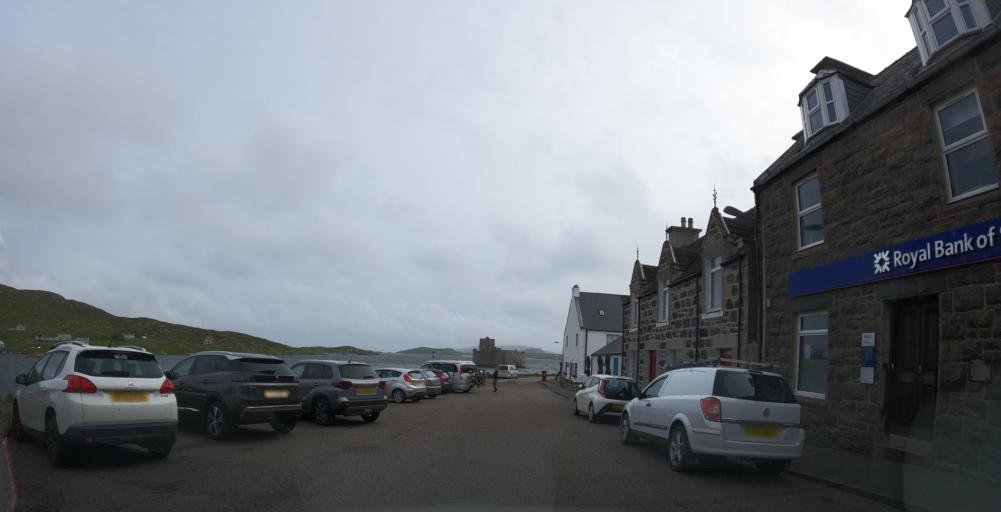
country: GB
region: Scotland
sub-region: Eilean Siar
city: Barra
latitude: 56.9546
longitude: -7.4863
